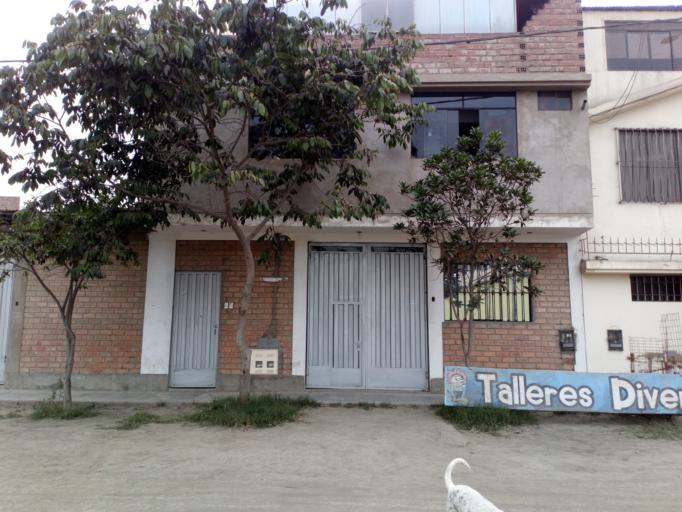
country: PE
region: Lima
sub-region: Lima
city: Urb. Santo Domingo
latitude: -11.9053
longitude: -77.0454
